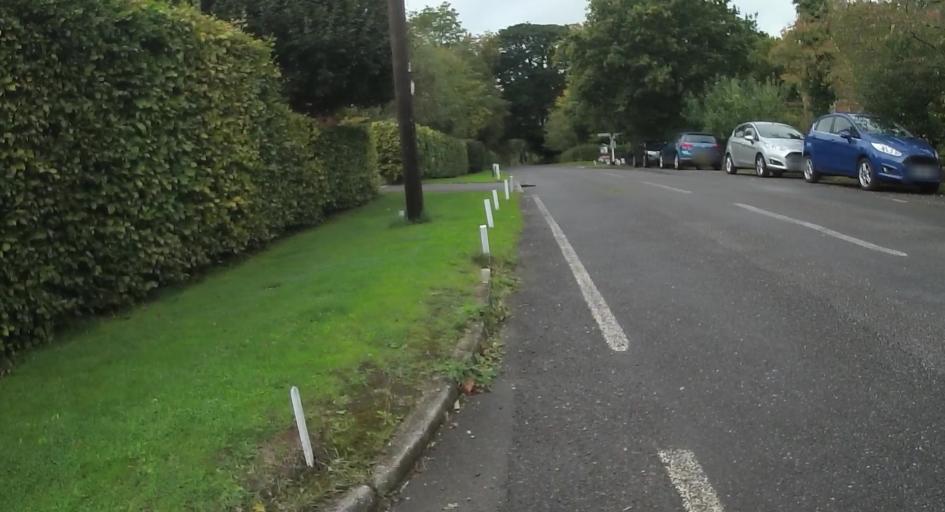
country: GB
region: England
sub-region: Hampshire
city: Tadley
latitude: 51.3125
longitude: -1.1554
